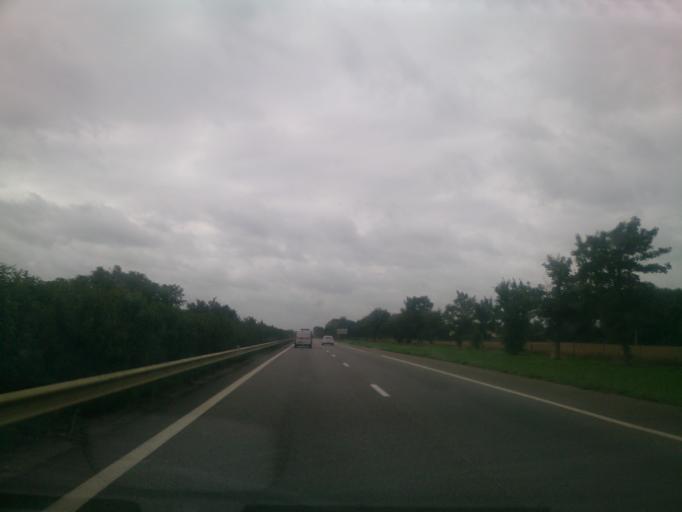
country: FR
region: Midi-Pyrenees
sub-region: Departement de la Haute-Garonne
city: Le Fauga
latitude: 43.3984
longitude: 1.2890
